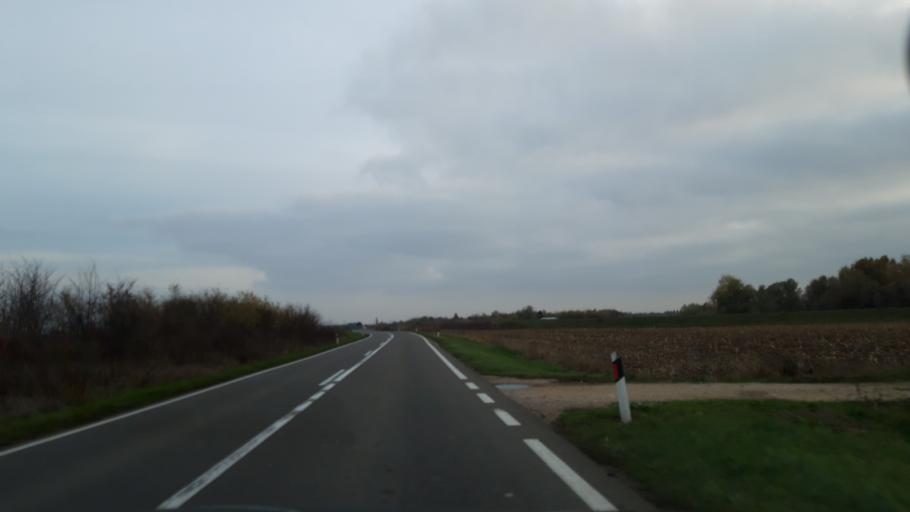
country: RS
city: Sanad
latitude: 45.9906
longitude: 20.1083
